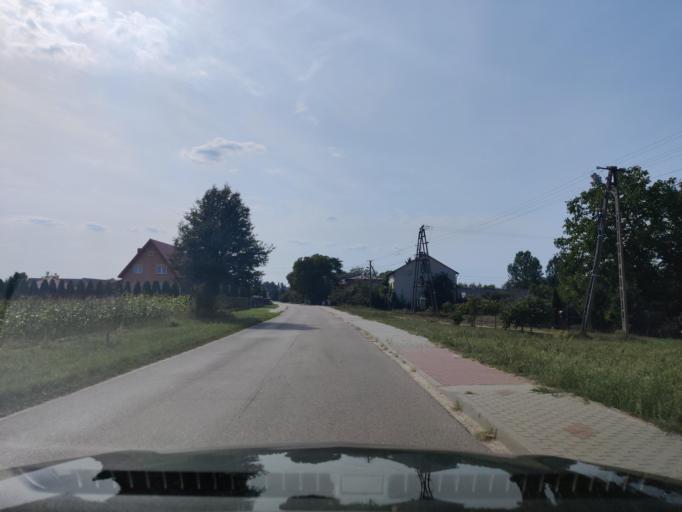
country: PL
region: Masovian Voivodeship
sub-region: Powiat wyszkowski
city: Rzasnik
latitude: 52.7651
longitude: 21.3641
